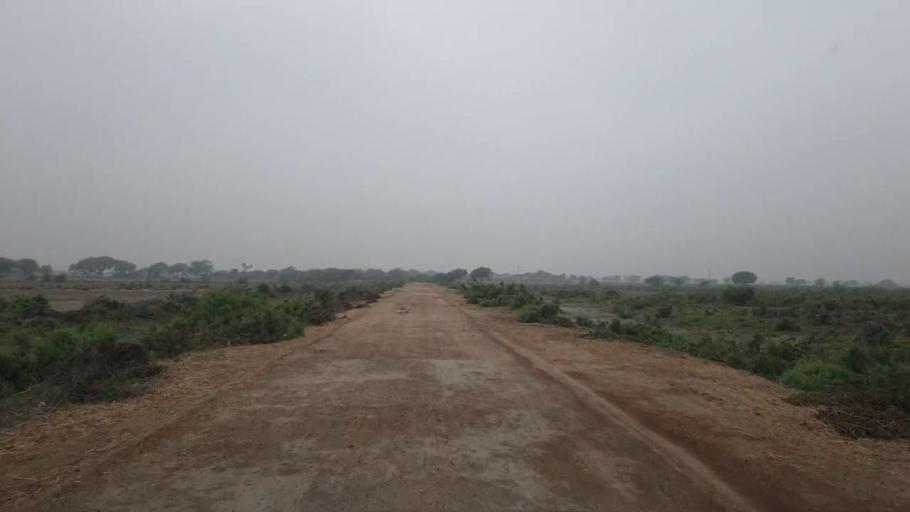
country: PK
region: Sindh
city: Badin
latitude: 24.6000
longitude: 68.6639
